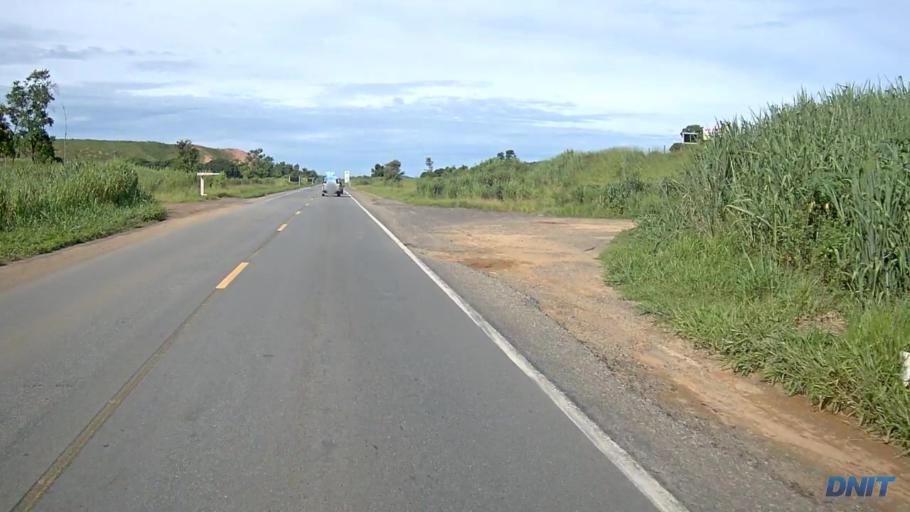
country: BR
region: Minas Gerais
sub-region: Belo Oriente
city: Belo Oriente
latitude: -19.1910
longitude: -42.2736
